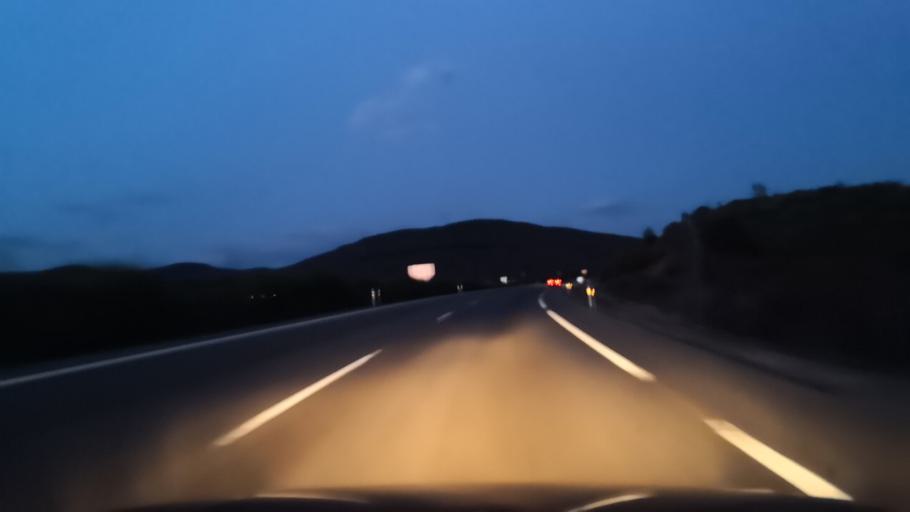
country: ES
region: Castille and Leon
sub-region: Provincia de Leon
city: Folgoso de la Ribera
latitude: 42.6231
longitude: -6.3199
